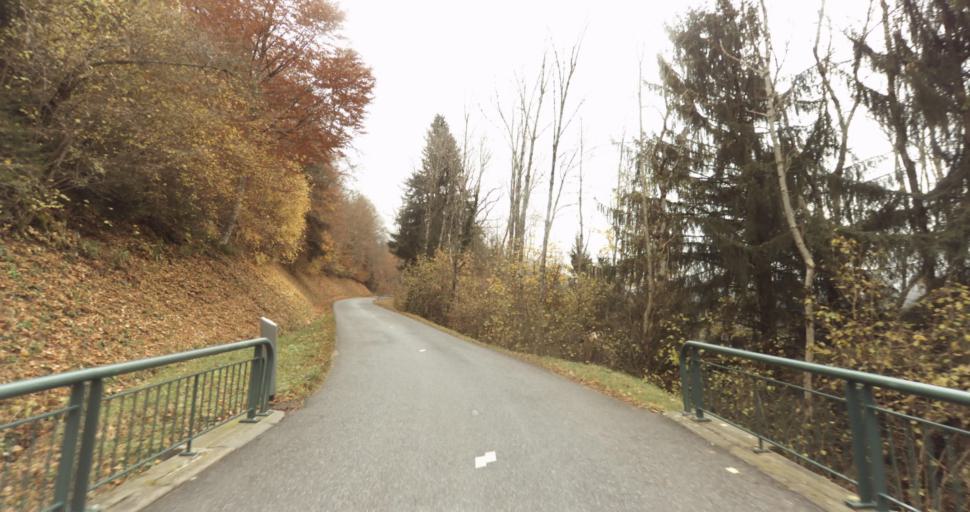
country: FR
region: Rhone-Alpes
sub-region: Departement de la Haute-Savoie
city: Thorens-Glieres
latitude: 45.9739
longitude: 6.2920
